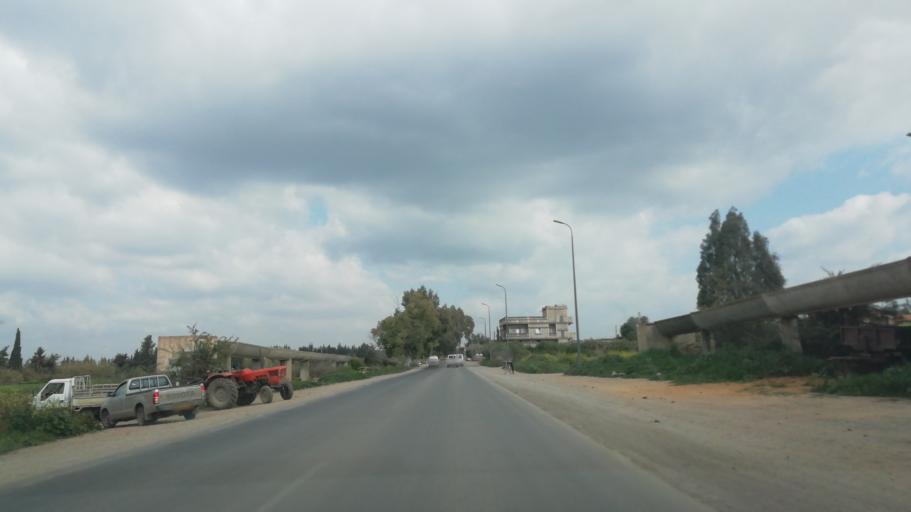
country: DZ
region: Mascara
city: Mascara
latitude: 35.6257
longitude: 0.1223
